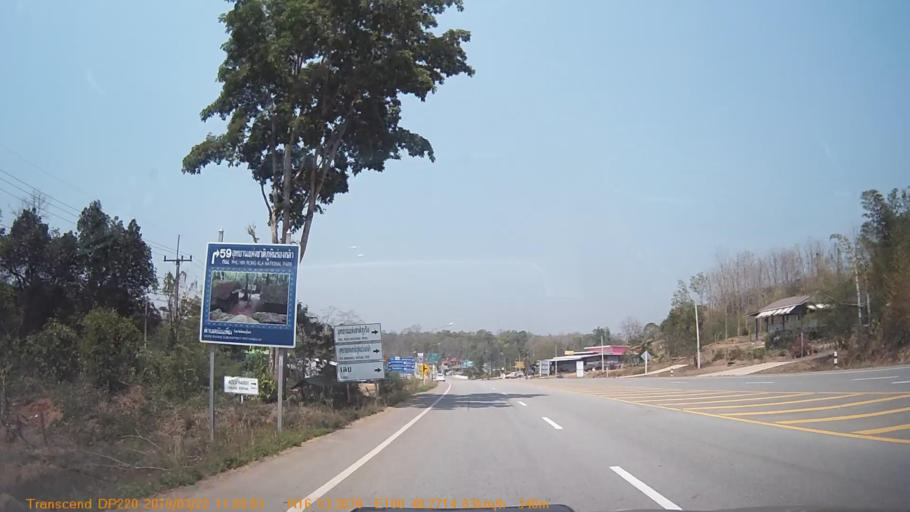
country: TH
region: Phitsanulok
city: Nakhon Thai
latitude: 16.8885
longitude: 100.8043
